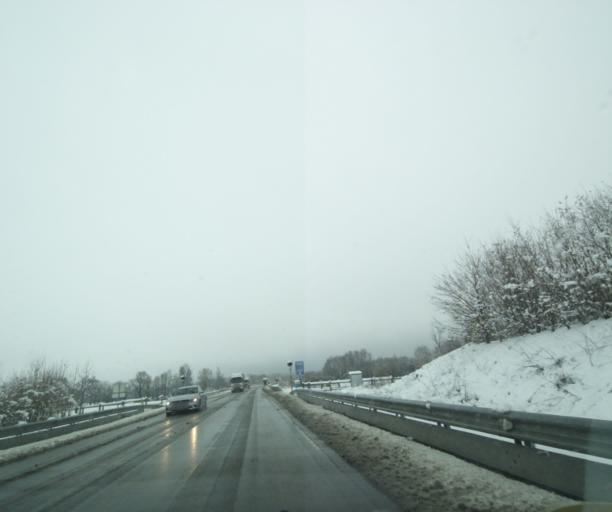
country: FR
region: Champagne-Ardenne
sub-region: Departement de la Haute-Marne
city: Saint-Dizier
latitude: 48.5813
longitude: 4.8865
